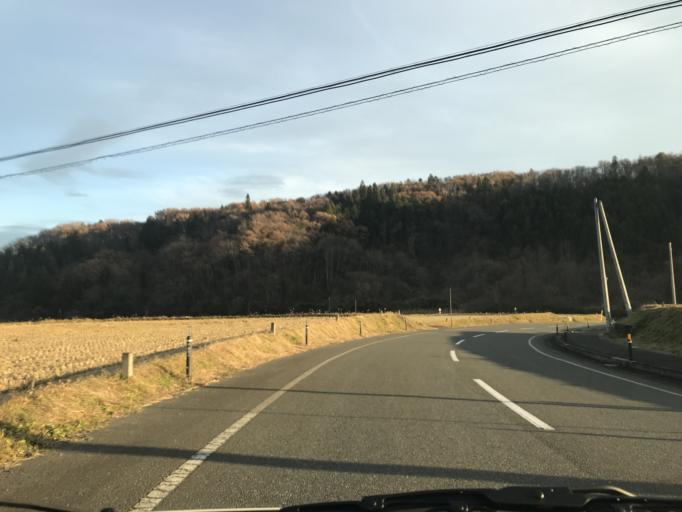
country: JP
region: Iwate
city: Ichinoseki
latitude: 38.9721
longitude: 141.0756
